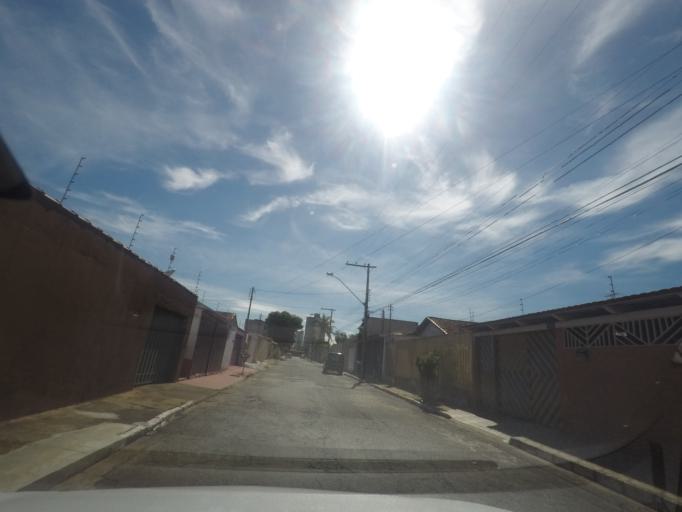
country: BR
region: Goias
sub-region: Goiania
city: Goiania
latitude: -16.6669
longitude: -49.2645
